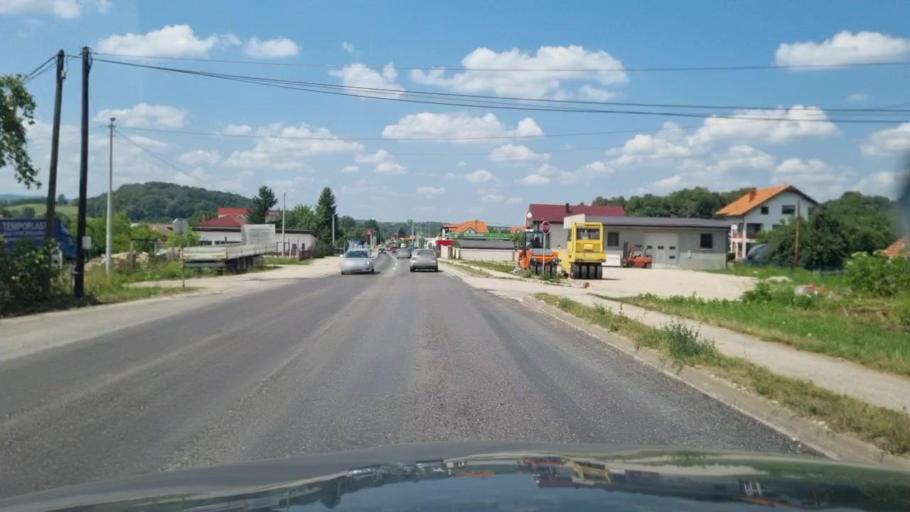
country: BA
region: Federation of Bosnia and Herzegovina
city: Srebrenik
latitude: 44.7184
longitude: 18.4886
